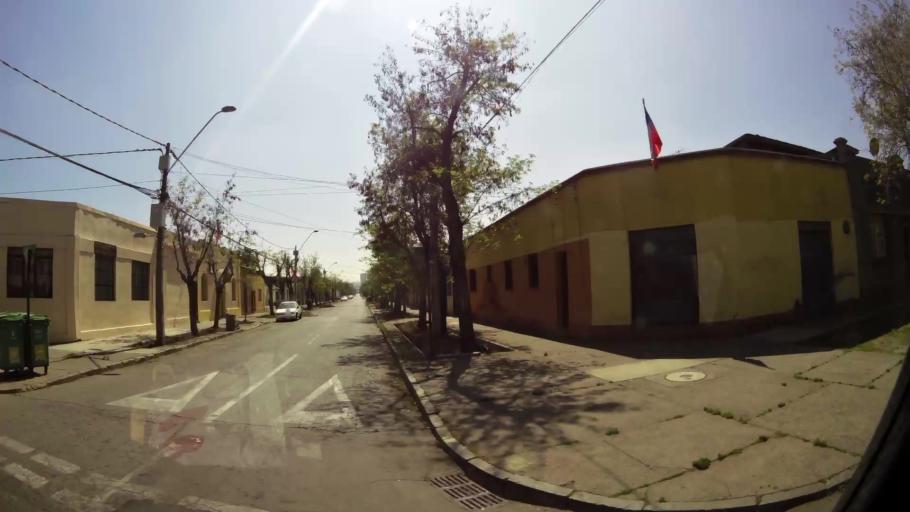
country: CL
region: Santiago Metropolitan
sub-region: Provincia de Santiago
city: Santiago
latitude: -33.4714
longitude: -70.6368
